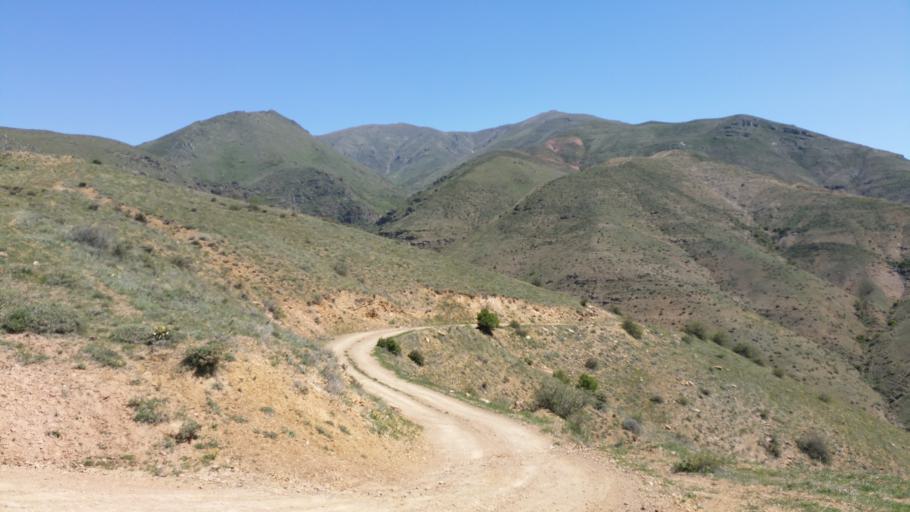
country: AM
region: Vayots' Dzori Marz
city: Vernashen
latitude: 39.7964
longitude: 45.3599
